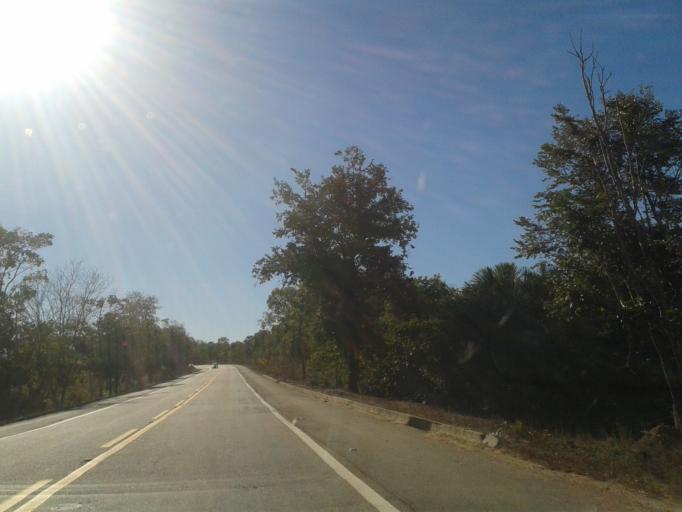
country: BR
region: Goias
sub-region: Itapuranga
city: Itapuranga
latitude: -15.3334
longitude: -50.4181
